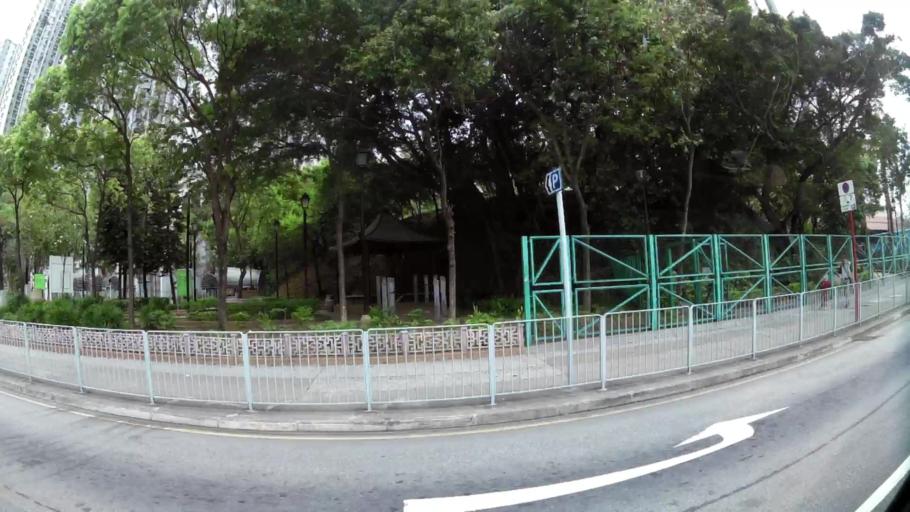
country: HK
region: Tuen Mun
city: Tuen Mun
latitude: 22.3829
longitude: 113.9752
